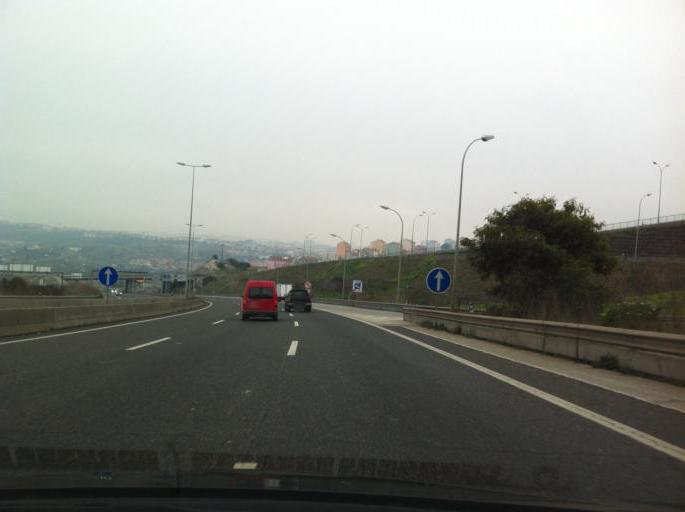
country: PT
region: Lisbon
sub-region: Odivelas
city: Famoes
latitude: 38.7727
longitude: -9.2193
